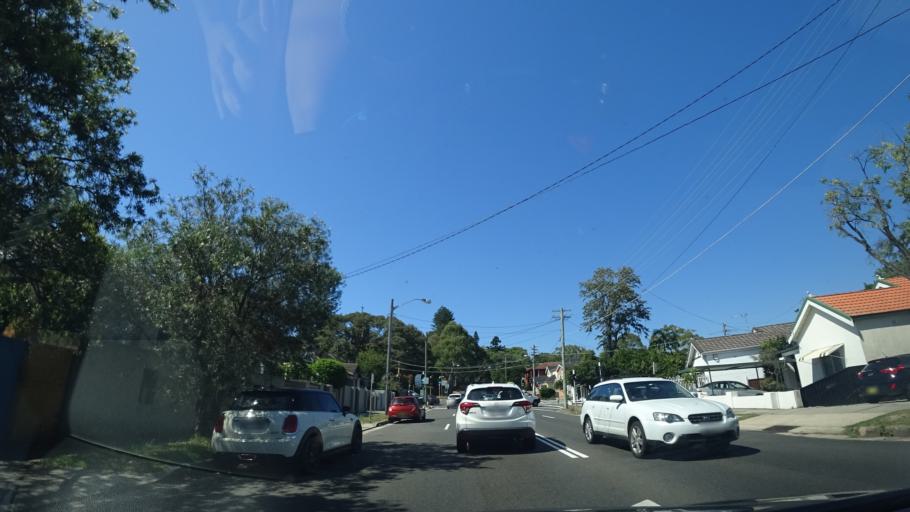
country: AU
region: New South Wales
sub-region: Randwick
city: Randwick
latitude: -33.9041
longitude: 151.2445
